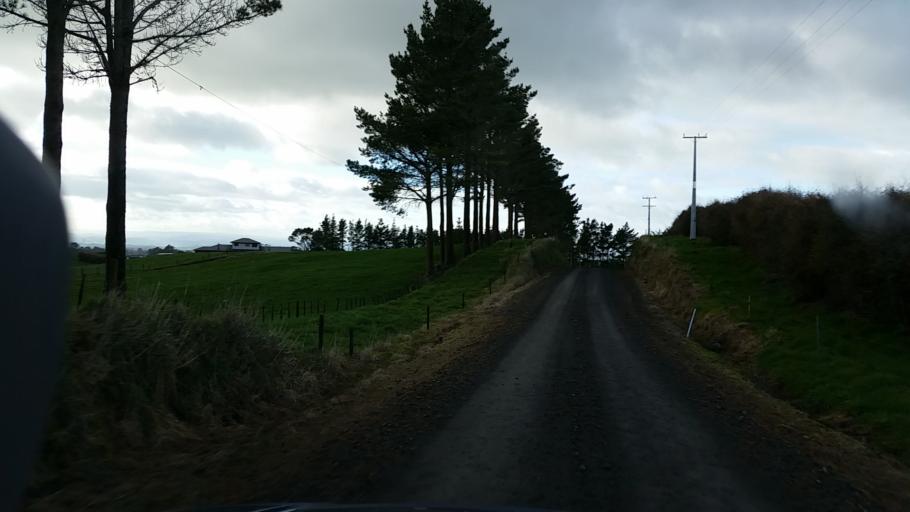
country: NZ
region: Taranaki
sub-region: South Taranaki District
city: Eltham
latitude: -39.3372
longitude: 174.1840
